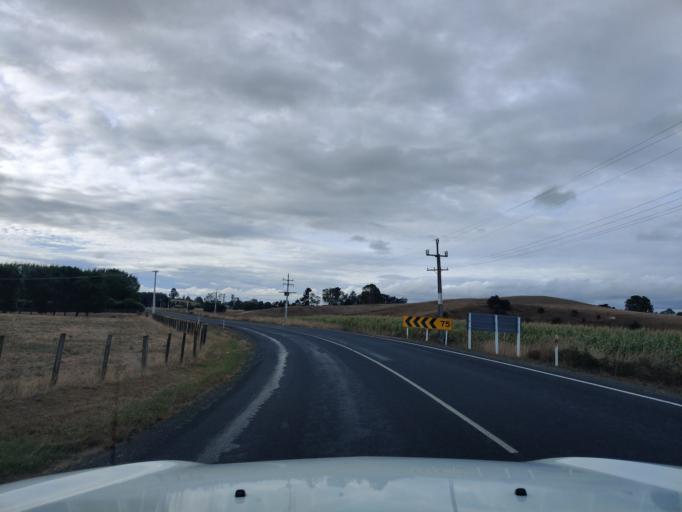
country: NZ
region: Waikato
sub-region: Waipa District
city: Cambridge
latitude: -37.8127
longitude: 175.4536
